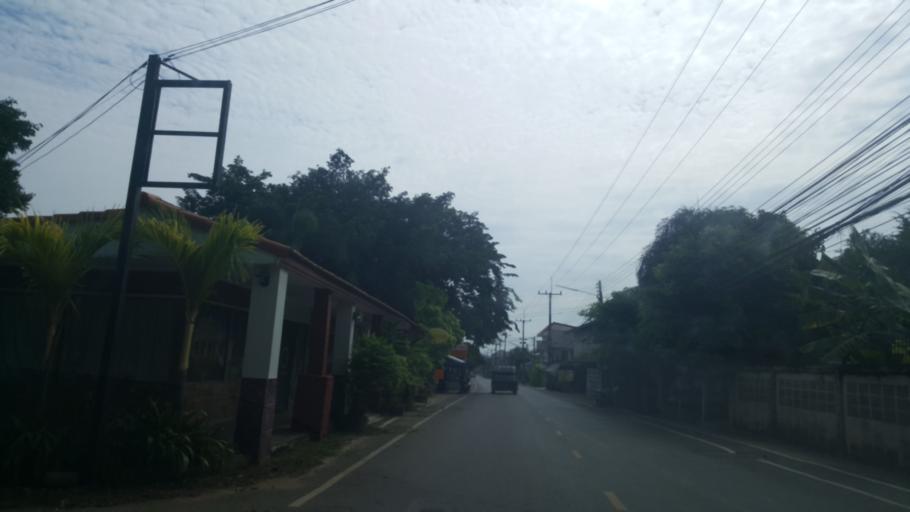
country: TH
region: Chon Buri
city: Sattahip
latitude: 12.6854
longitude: 100.9051
